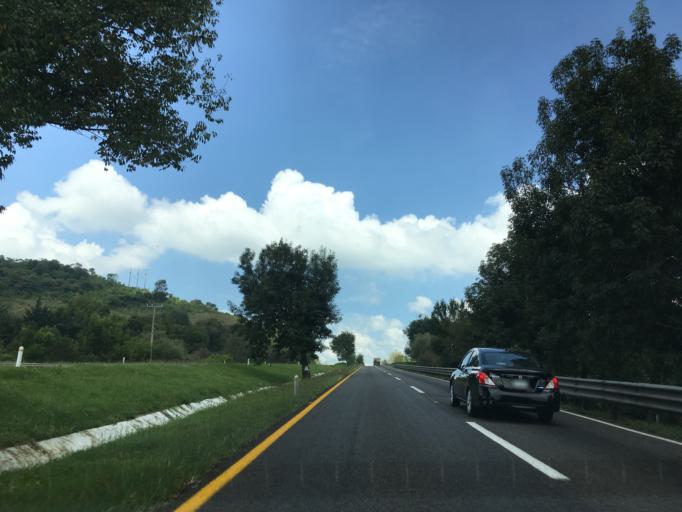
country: MX
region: Michoacan
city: Lagunillas
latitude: 19.5582
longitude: -101.3974
